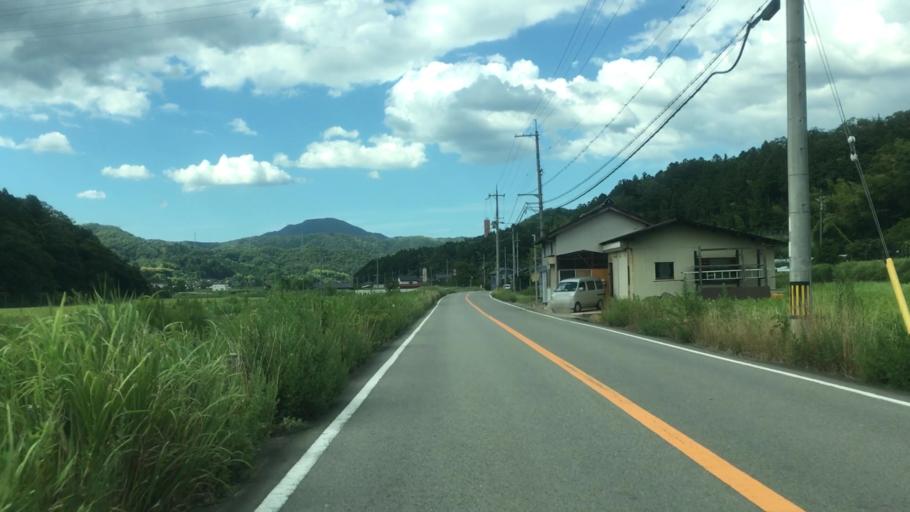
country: JP
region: Hyogo
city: Toyooka
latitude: 35.5380
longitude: 134.7899
